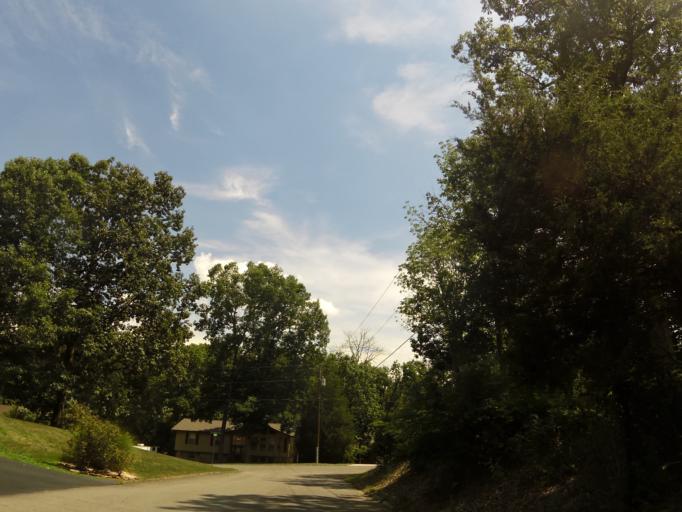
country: US
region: Tennessee
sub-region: Knox County
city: Knoxville
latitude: 35.9174
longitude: -83.8324
